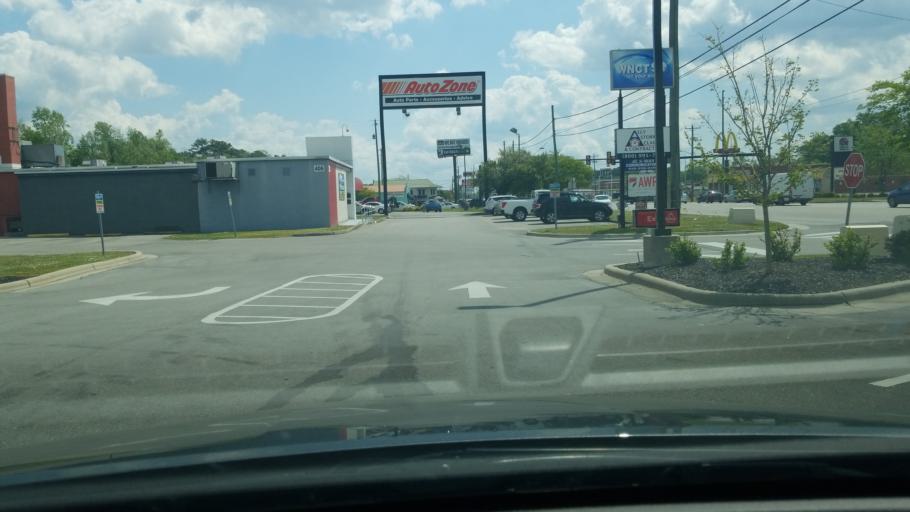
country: US
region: North Carolina
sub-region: Onslow County
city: Jacksonville
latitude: 34.7523
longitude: -77.4473
